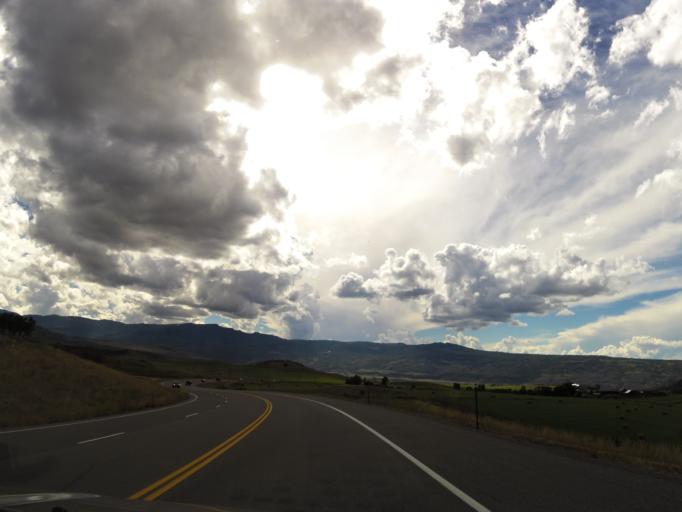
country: US
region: Colorado
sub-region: Hinsdale County
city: Lake City
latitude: 38.3957
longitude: -107.4682
